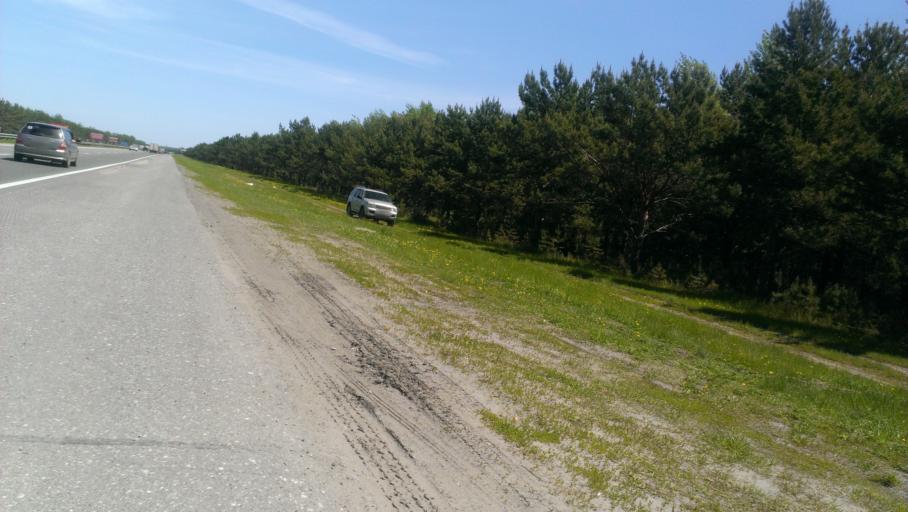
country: RU
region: Altai Krai
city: Zaton
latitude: 53.3182
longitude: 83.8758
